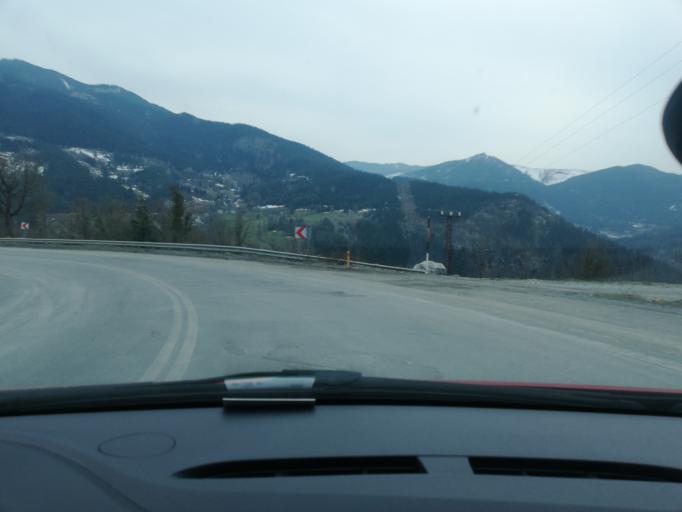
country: TR
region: Kastamonu
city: Kure
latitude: 41.8464
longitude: 33.7219
